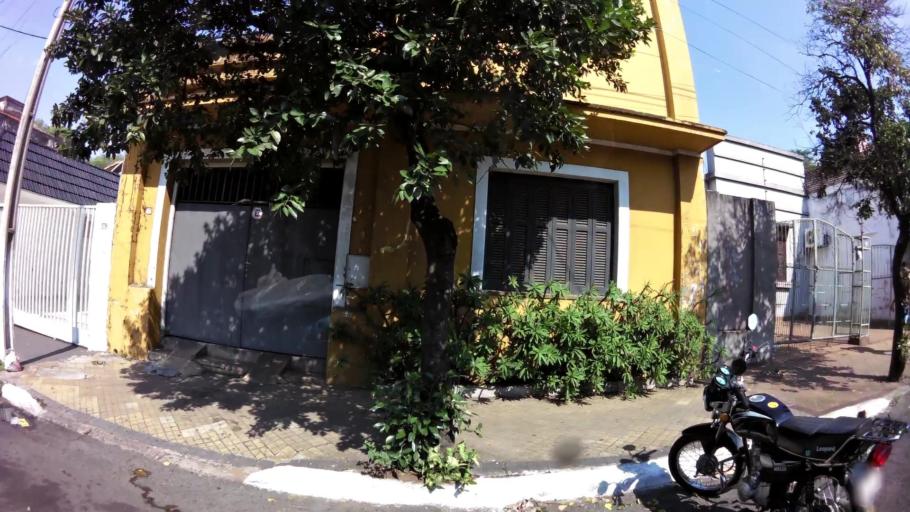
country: PY
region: Asuncion
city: Asuncion
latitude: -25.2939
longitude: -57.6307
